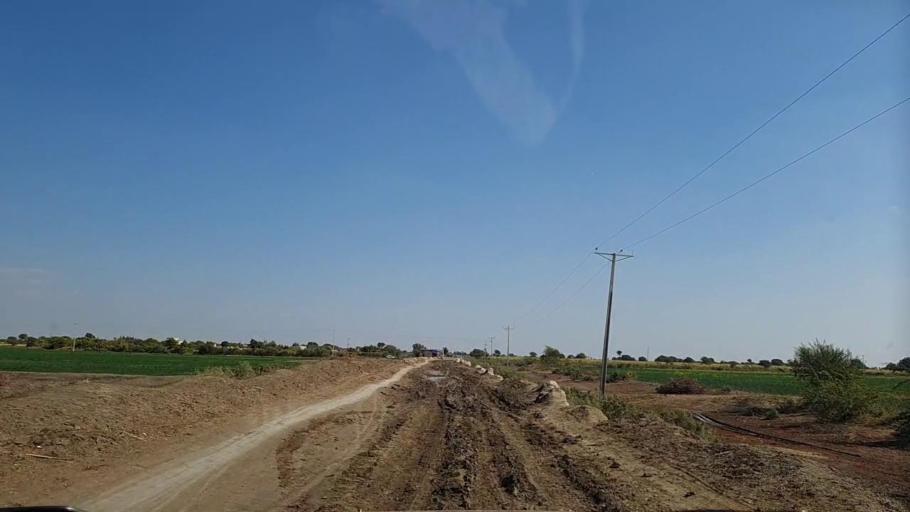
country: PK
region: Sindh
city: Pithoro
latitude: 25.6895
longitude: 69.4364
